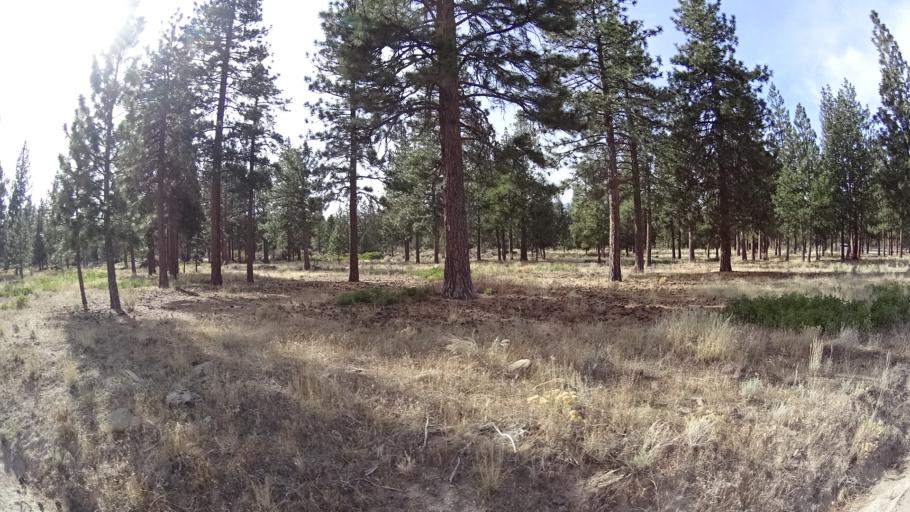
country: US
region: California
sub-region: Siskiyou County
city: Weed
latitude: 41.4918
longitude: -122.3728
